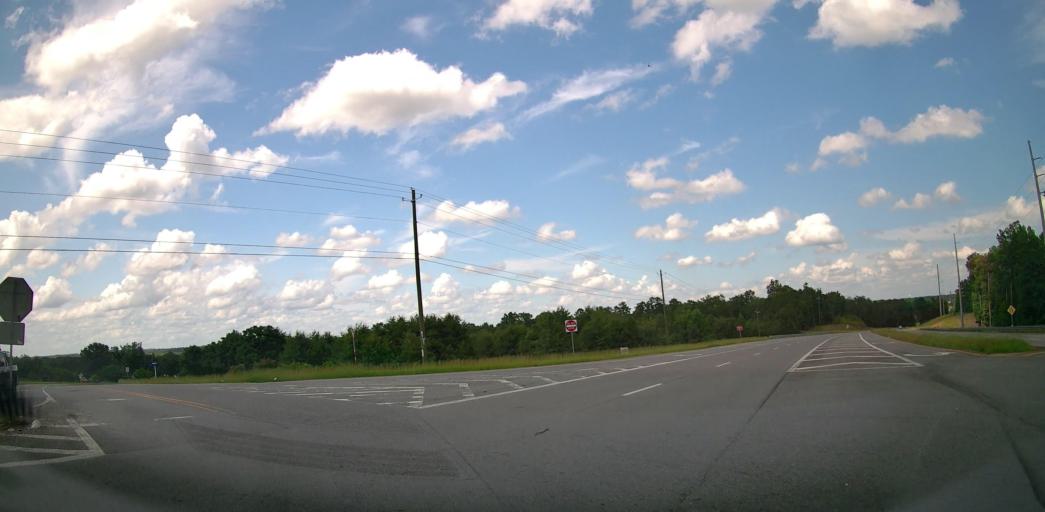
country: US
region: Georgia
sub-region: Houston County
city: Centerville
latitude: 32.6797
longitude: -83.6997
